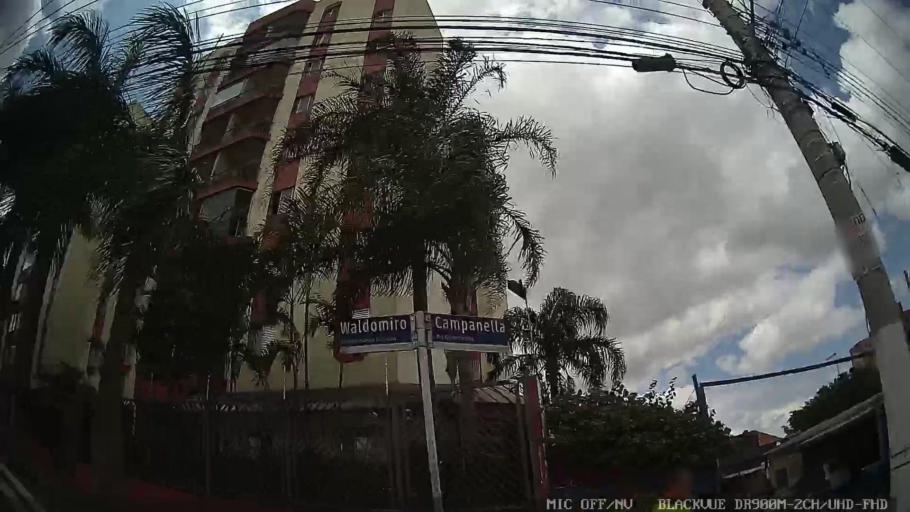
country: BR
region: Sao Paulo
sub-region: Ferraz De Vasconcelos
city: Ferraz de Vasconcelos
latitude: -23.5334
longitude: -46.4599
